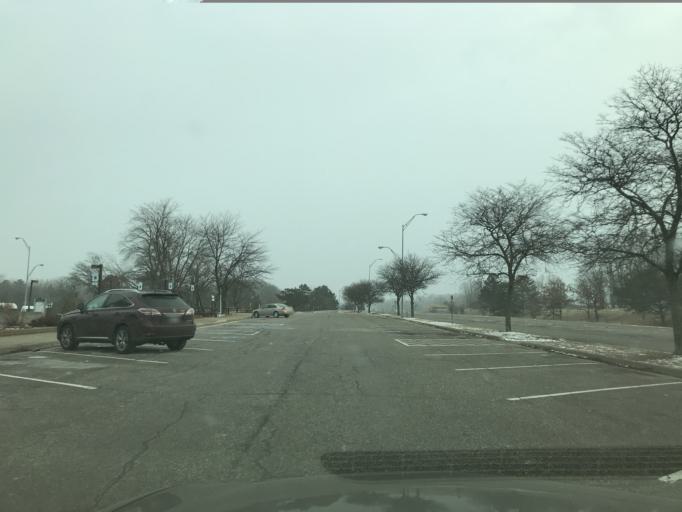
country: US
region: Michigan
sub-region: Clare County
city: Clare
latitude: 43.8505
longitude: -84.7771
